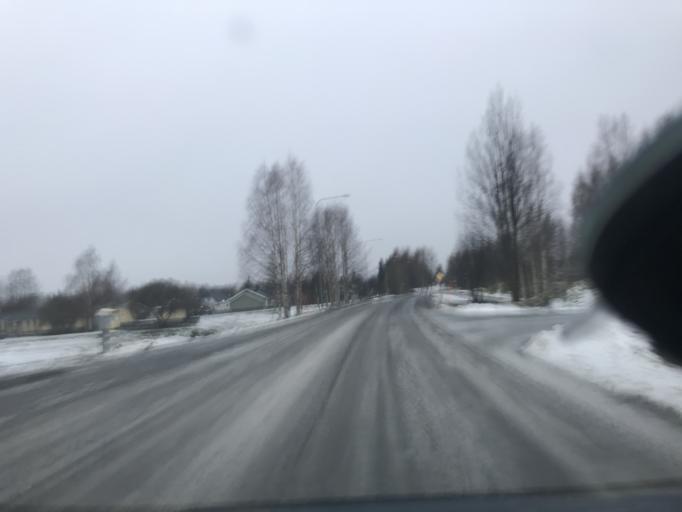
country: SE
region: Norrbotten
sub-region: Lulea Kommun
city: Sodra Sunderbyn
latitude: 65.6531
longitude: 21.9496
